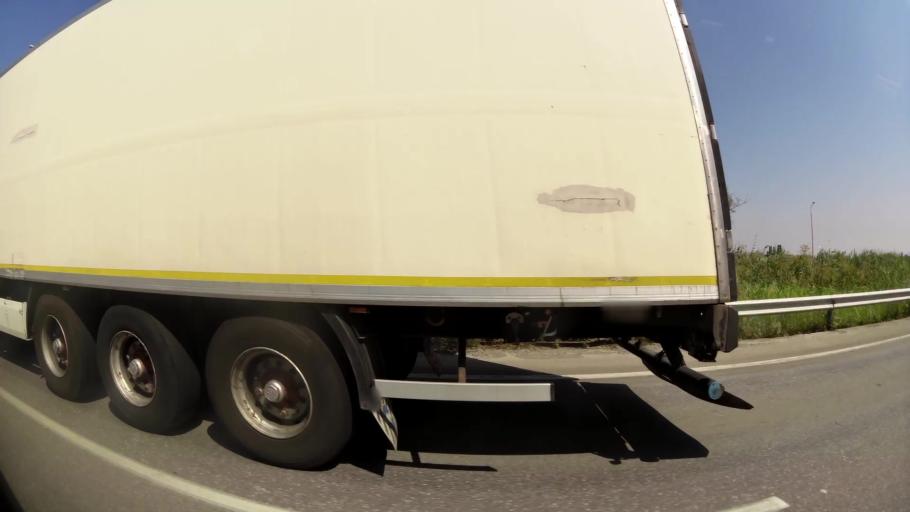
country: GR
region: Central Macedonia
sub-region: Nomos Thessalonikis
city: Chalastra
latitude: 40.6098
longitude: 22.7334
